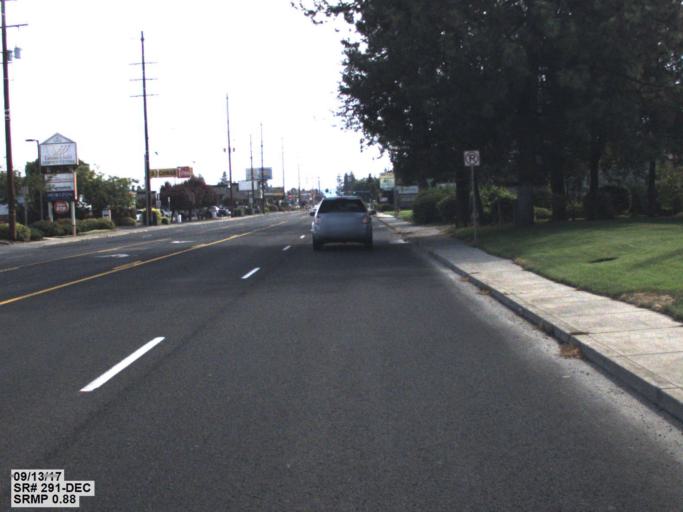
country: US
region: Washington
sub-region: Spokane County
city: Town and Country
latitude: 47.7153
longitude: -117.4300
